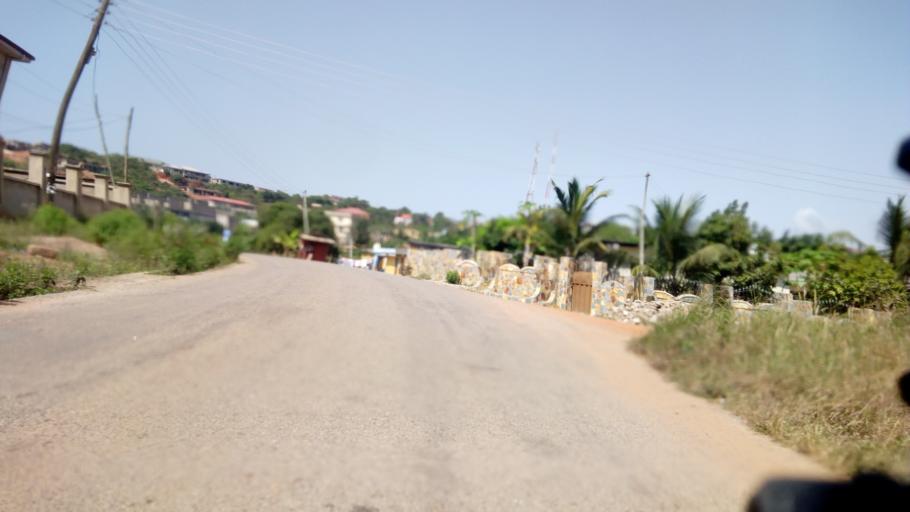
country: GH
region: Central
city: Cape Coast
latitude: 5.1129
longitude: -1.2715
